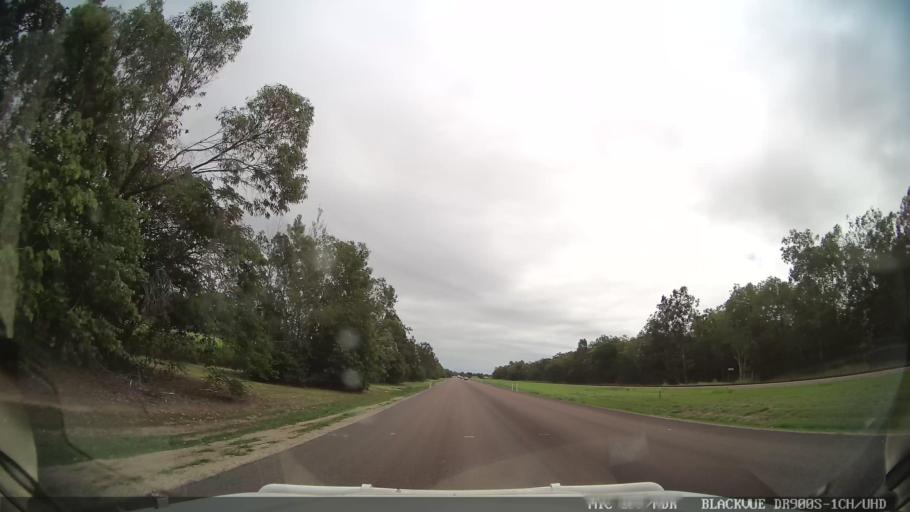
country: AU
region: Queensland
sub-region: Hinchinbrook
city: Ingham
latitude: -18.9285
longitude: 146.2650
